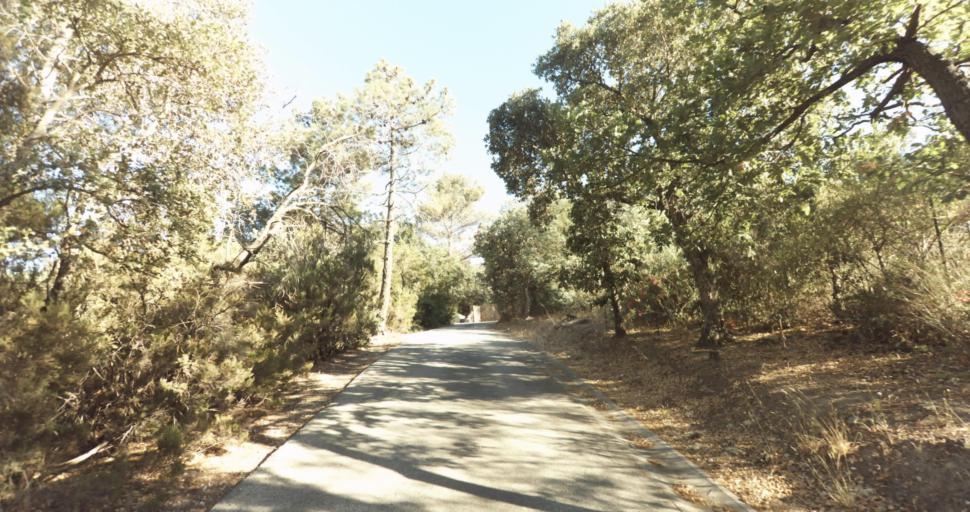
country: FR
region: Provence-Alpes-Cote d'Azur
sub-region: Departement du Var
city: Gassin
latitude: 43.2341
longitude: 6.6005
